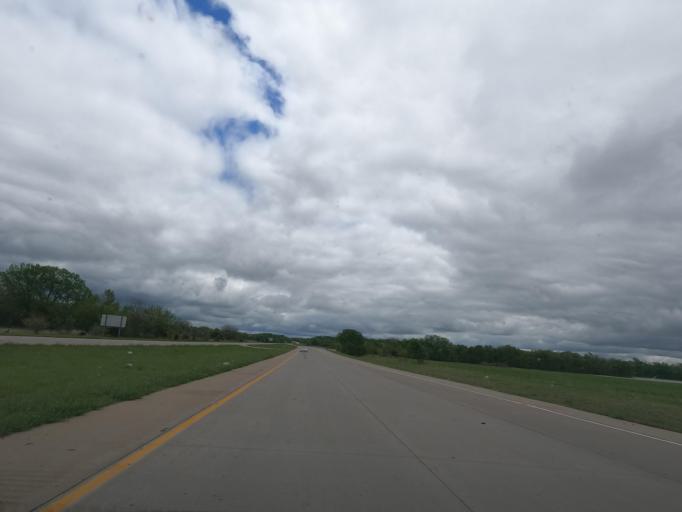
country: US
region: Kansas
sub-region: Wilson County
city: Neodesha
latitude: 37.3576
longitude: -95.6901
